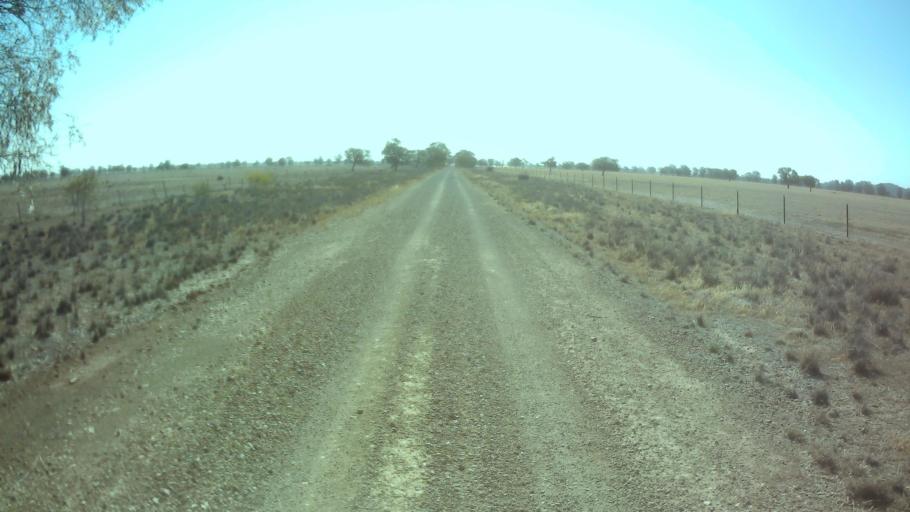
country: AU
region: New South Wales
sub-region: Weddin
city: Grenfell
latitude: -33.7594
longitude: 147.7048
